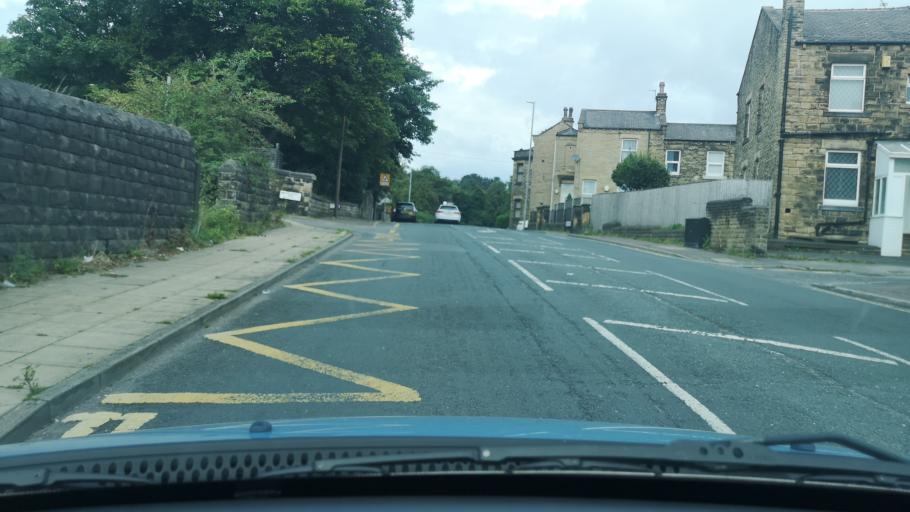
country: GB
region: England
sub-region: Kirklees
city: Batley
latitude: 53.7000
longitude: -1.6412
